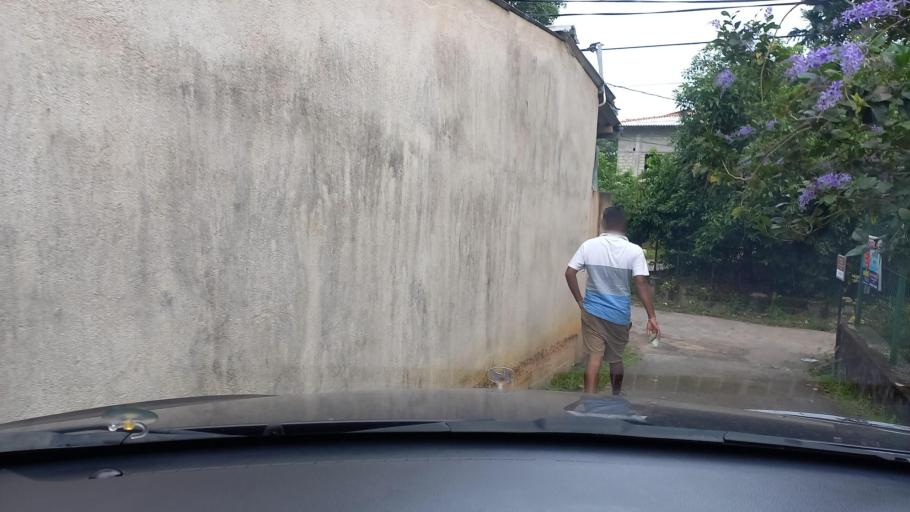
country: LK
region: Central
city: Kadugannawa
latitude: 7.2592
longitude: 80.3568
